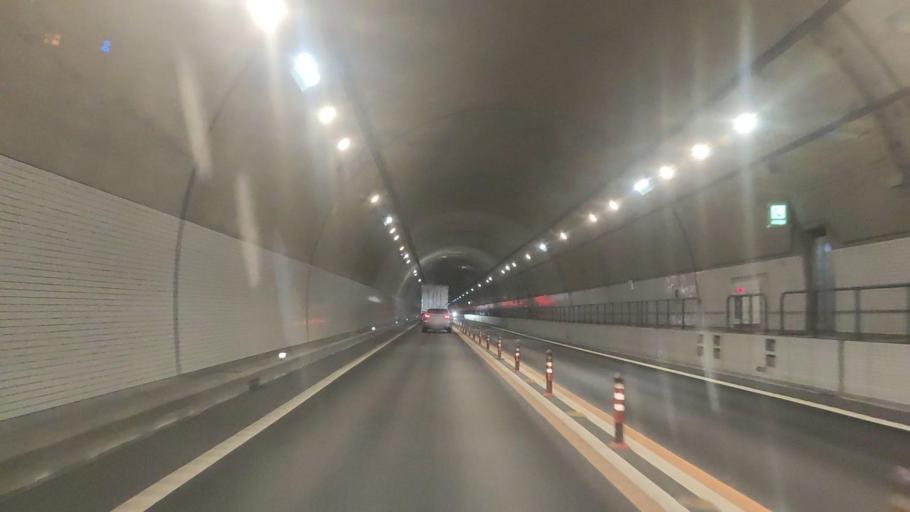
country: JP
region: Fukuoka
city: Yukuhashi
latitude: 33.7532
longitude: 130.9561
